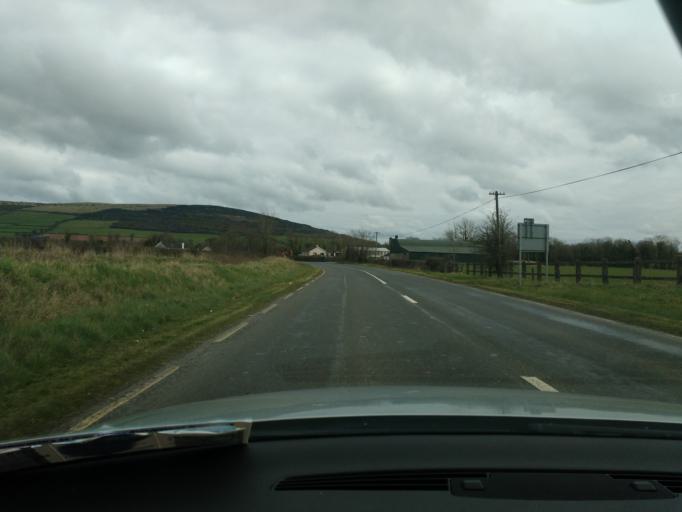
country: IE
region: Leinster
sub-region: Laois
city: Rathdowney
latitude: 52.7202
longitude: -7.5308
